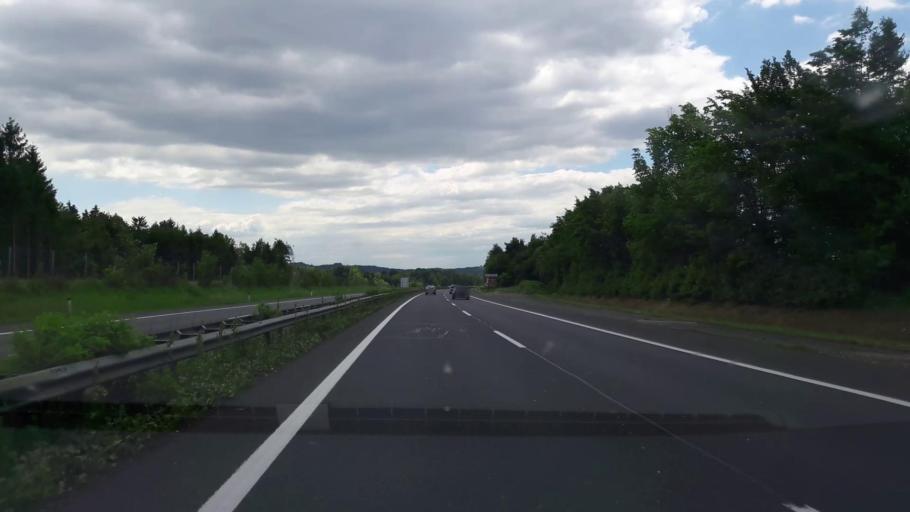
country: AT
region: Styria
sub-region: Politischer Bezirk Hartberg-Fuerstenfeld
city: Hainersdorf
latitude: 47.1042
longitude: 15.9848
